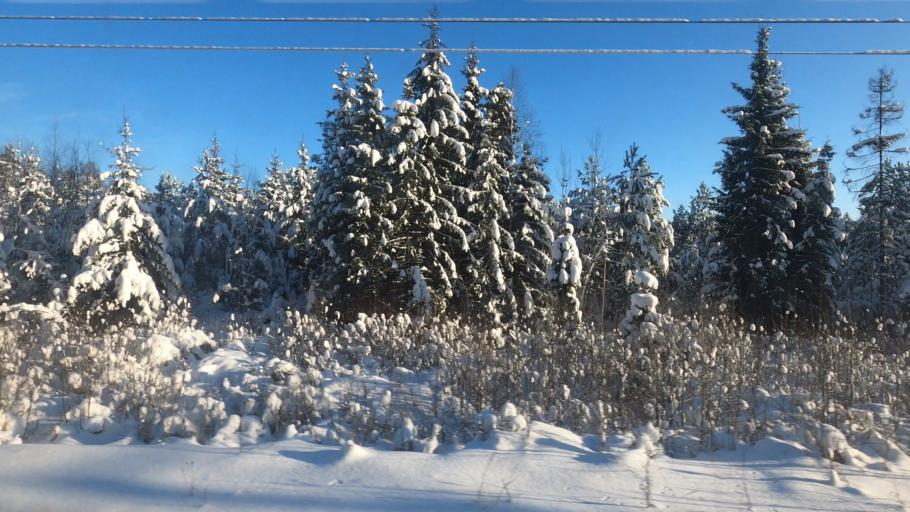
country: RU
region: Moskovskaya
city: Verbilki
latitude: 56.5311
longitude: 37.5598
